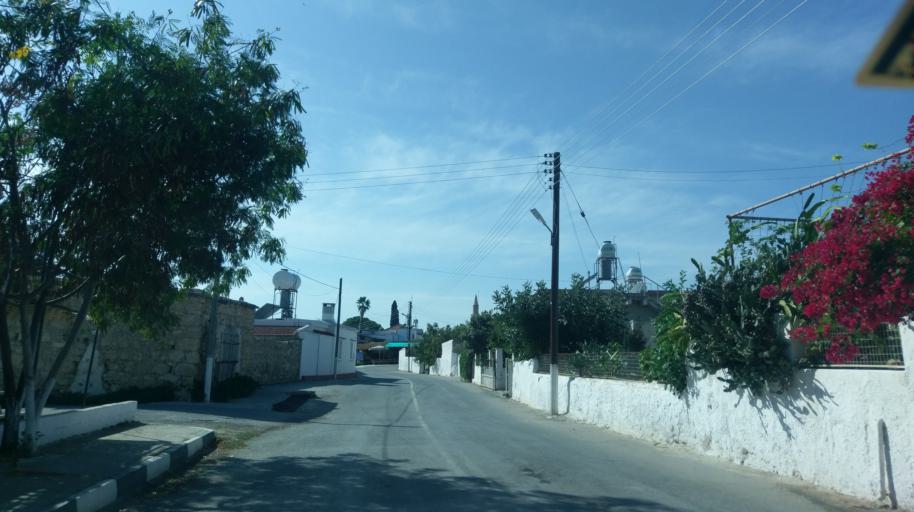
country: CY
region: Ammochostos
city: Leonarisso
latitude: 35.4118
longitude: 33.9986
